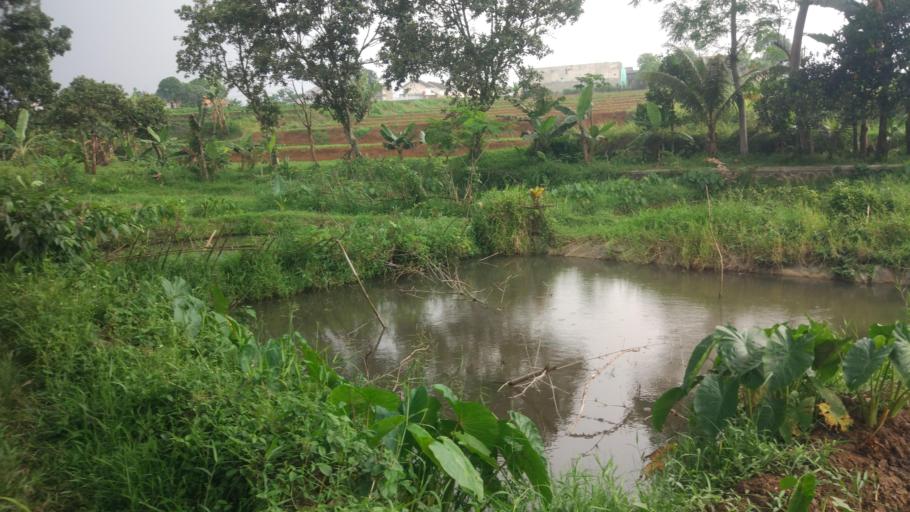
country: ID
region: West Java
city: Ciampea
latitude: -6.5344
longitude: 106.7288
